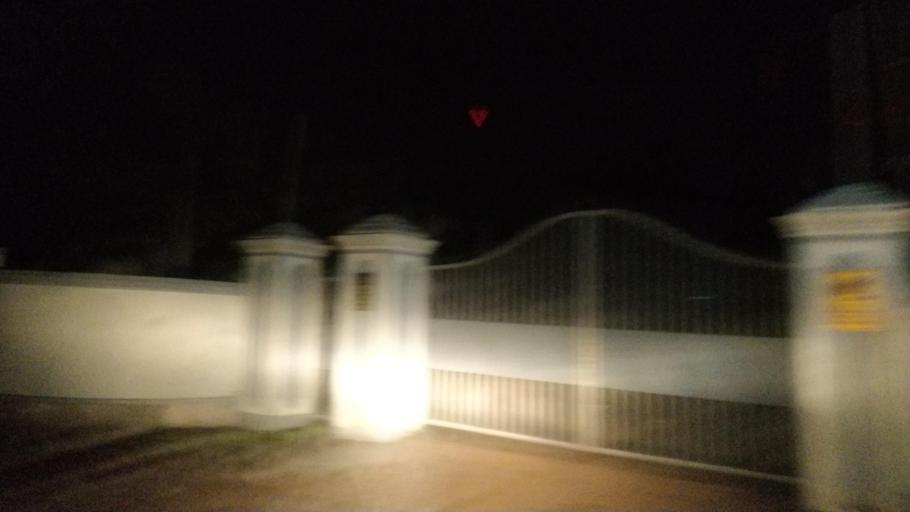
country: IN
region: Kerala
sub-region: Kottayam
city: Kottayam
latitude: 9.6407
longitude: 76.5080
